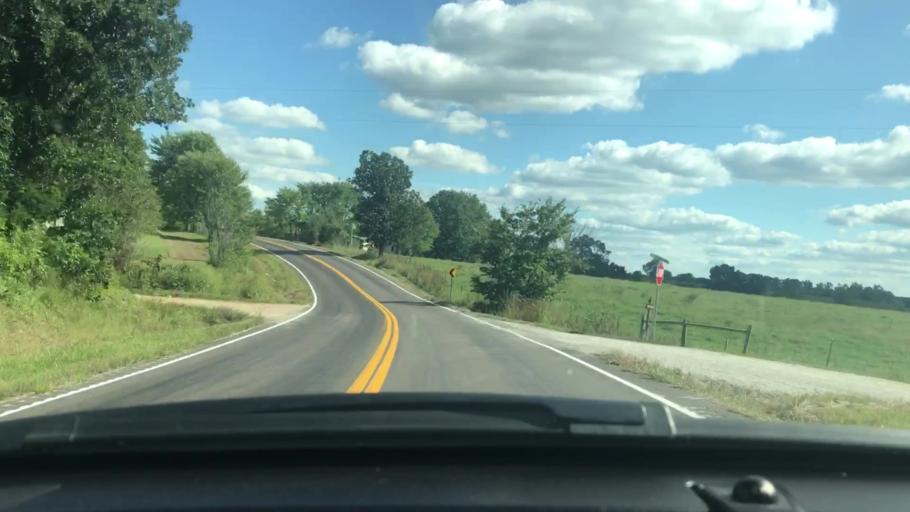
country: US
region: Missouri
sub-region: Wright County
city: Mountain Grove
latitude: 37.2559
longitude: -92.3078
